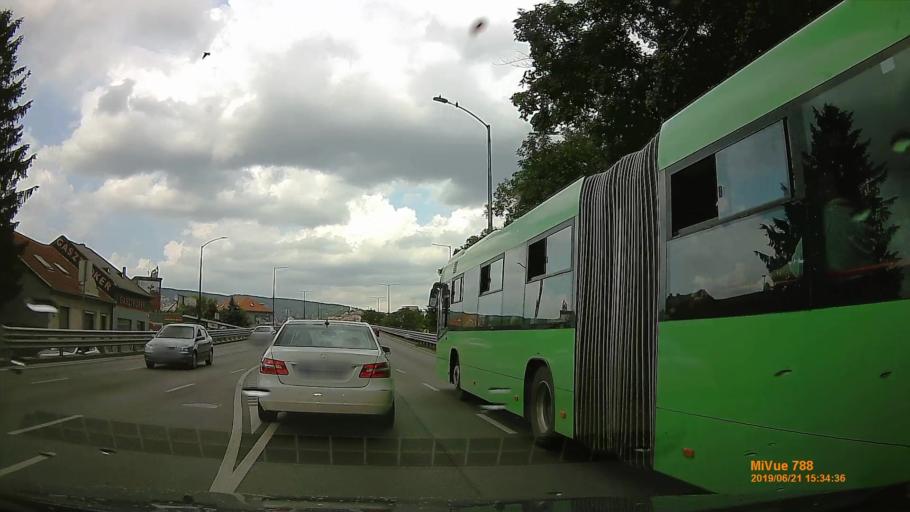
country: HU
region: Baranya
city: Pecs
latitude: 46.0649
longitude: 18.2317
